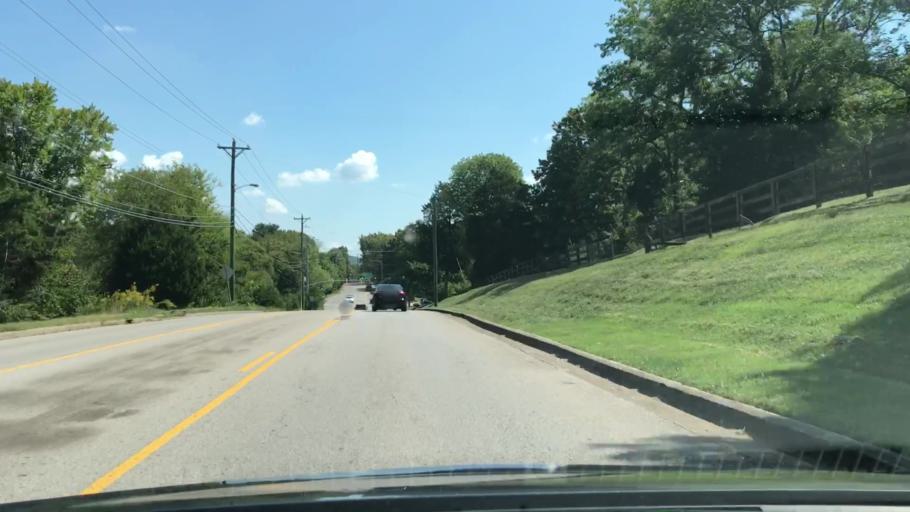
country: US
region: Tennessee
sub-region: Williamson County
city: Brentwood Estates
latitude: 36.0327
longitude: -86.7710
